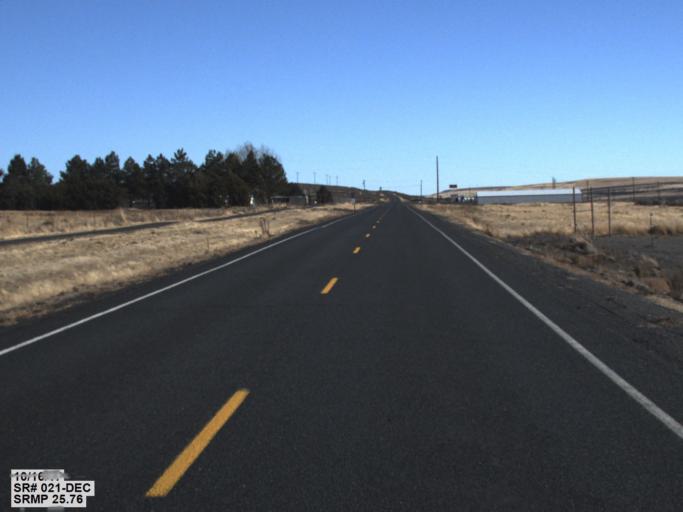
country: US
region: Washington
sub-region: Adams County
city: Ritzville
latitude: 46.9706
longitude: -118.5960
